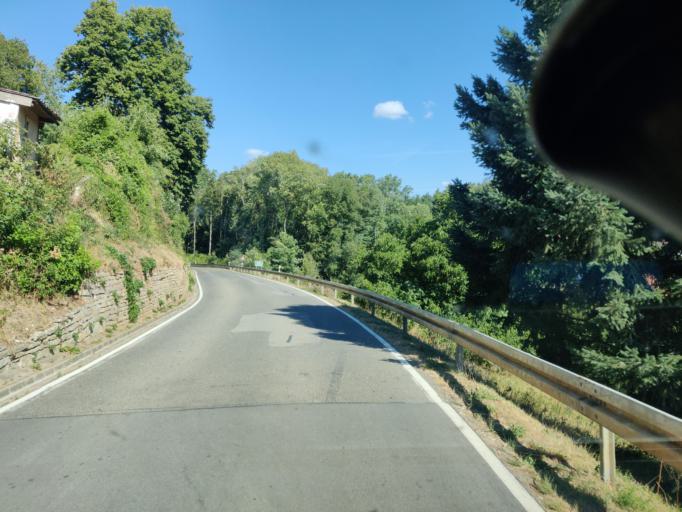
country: DE
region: Bavaria
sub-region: Regierungsbezirk Mittelfranken
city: Bergen
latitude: 49.0715
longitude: 11.0847
